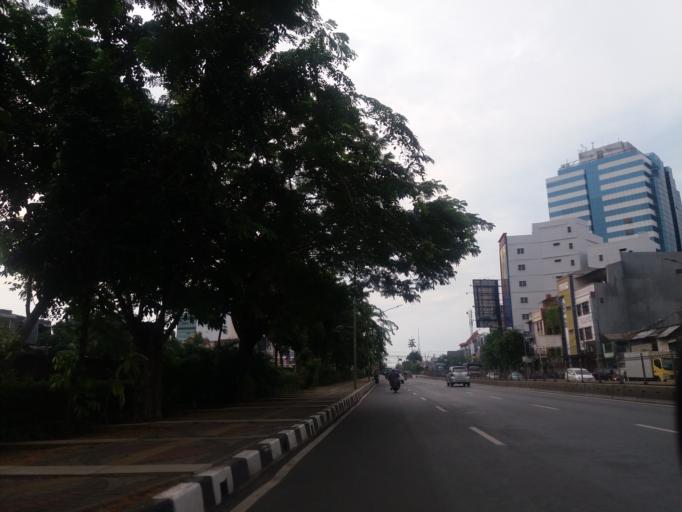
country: ID
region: Jakarta Raya
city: Jakarta
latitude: -6.1434
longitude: 106.8337
